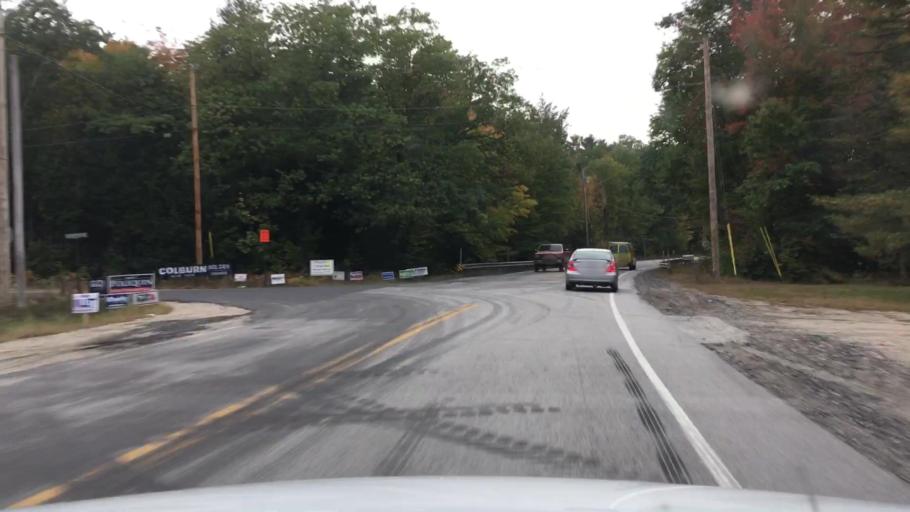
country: US
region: Maine
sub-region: Cumberland County
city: Harrison
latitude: 44.2125
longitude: -70.6792
